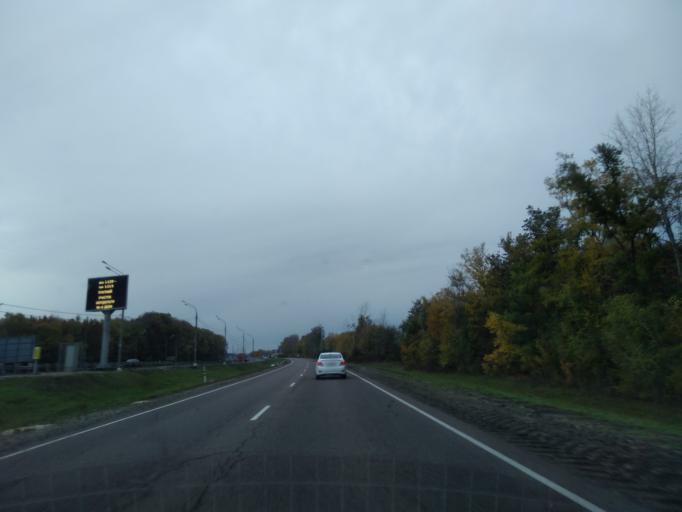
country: RU
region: Lipetsk
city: Zadonsk
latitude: 52.4397
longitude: 38.8073
